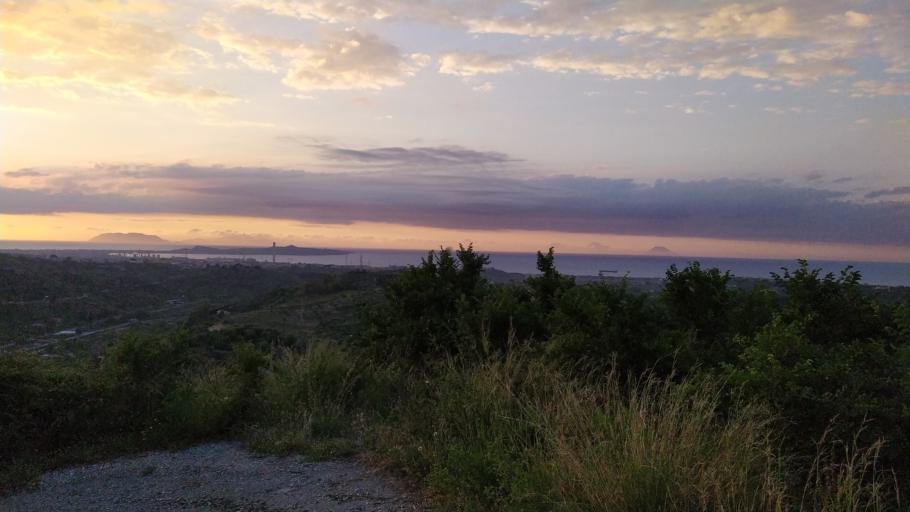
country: IT
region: Sicily
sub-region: Messina
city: Condro
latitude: 38.1635
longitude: 15.3301
